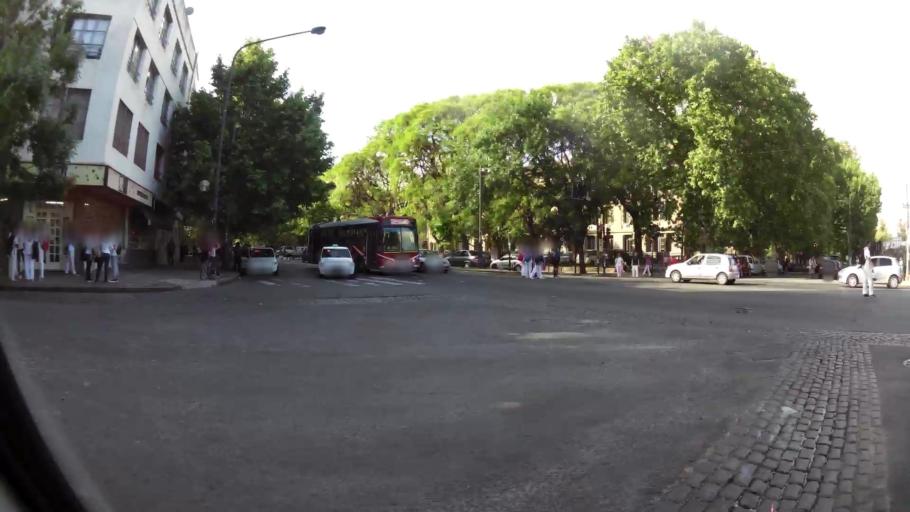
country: AR
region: Buenos Aires
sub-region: Partido de La Plata
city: La Plata
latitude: -34.9093
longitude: -57.9436
